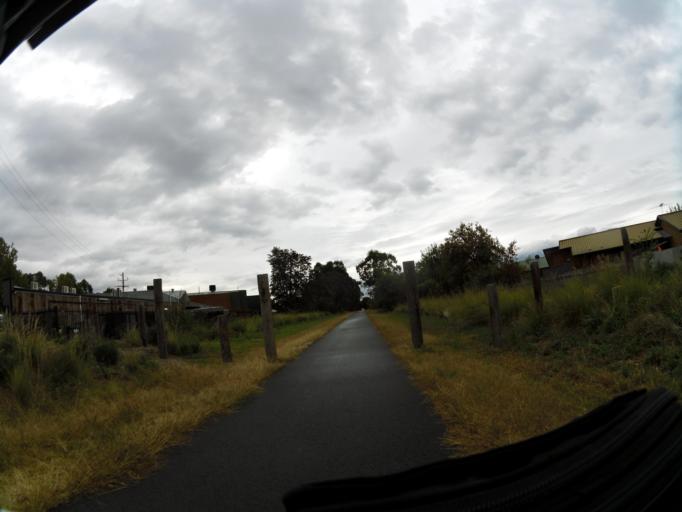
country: AU
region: Victoria
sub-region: Wodonga
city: Wodonga
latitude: -36.1290
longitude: 146.8963
